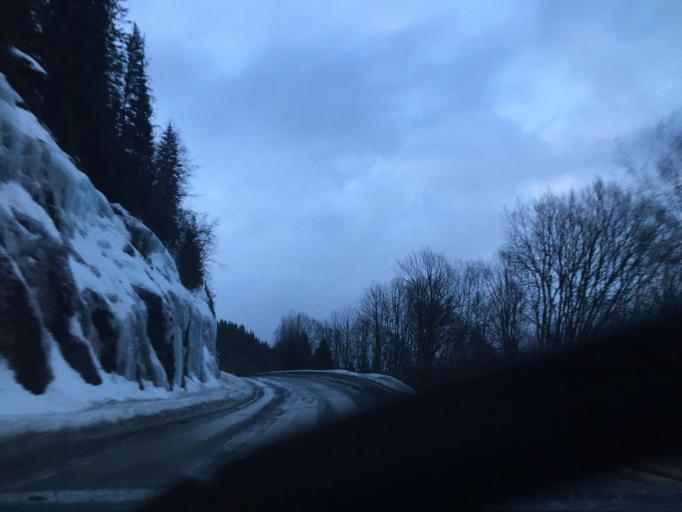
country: NO
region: Nordland
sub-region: Rana
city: Hauknes
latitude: 66.2909
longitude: 13.9133
